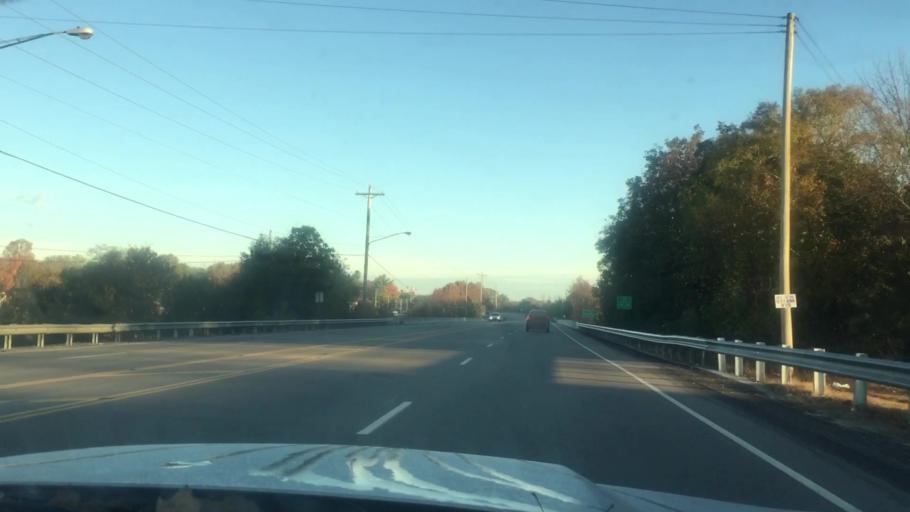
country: US
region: Tennessee
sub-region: Franklin County
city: Estill Springs
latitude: 35.2568
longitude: -86.1214
